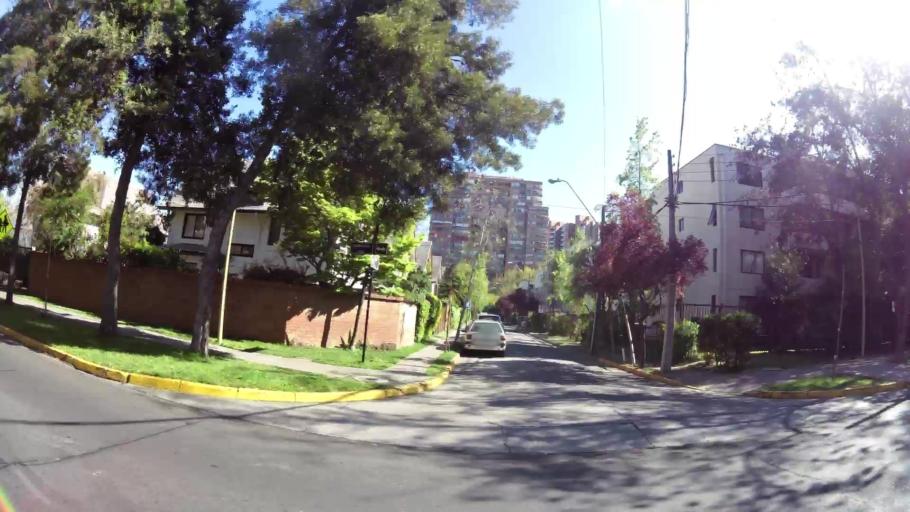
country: CL
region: Santiago Metropolitan
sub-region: Provincia de Santiago
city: Villa Presidente Frei, Nunoa, Santiago, Chile
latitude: -33.4026
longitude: -70.5628
